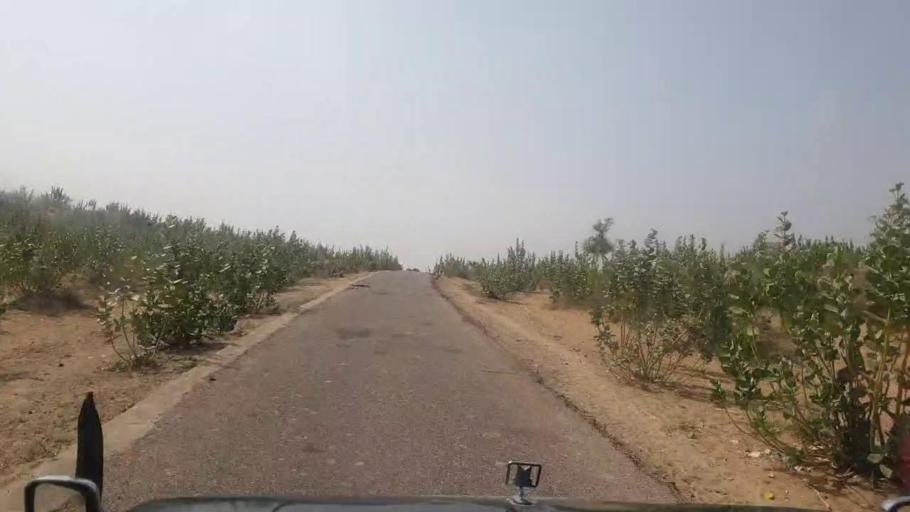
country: PK
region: Sindh
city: Islamkot
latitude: 25.0862
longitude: 70.1555
